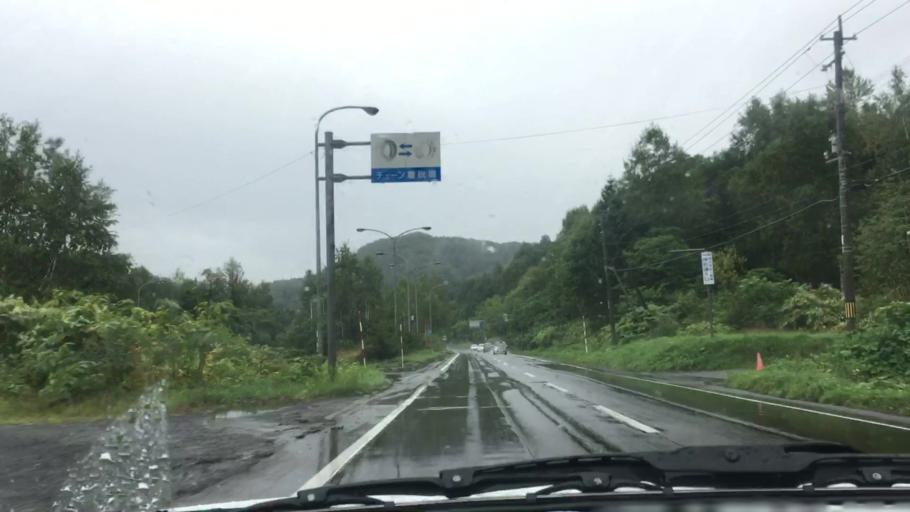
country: JP
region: Hokkaido
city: Niseko Town
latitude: 42.8287
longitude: 141.0073
